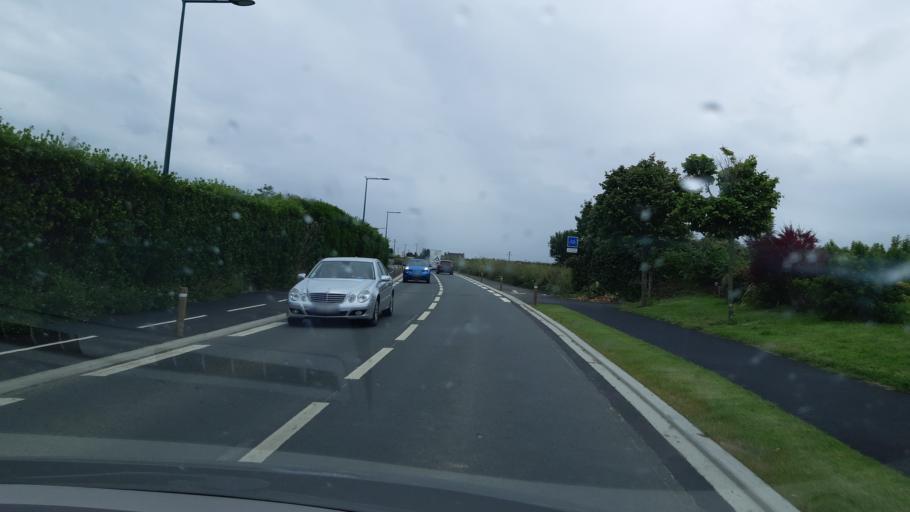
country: FR
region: Brittany
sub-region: Departement du Finistere
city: Roscoff
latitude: 48.7120
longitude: -3.9848
